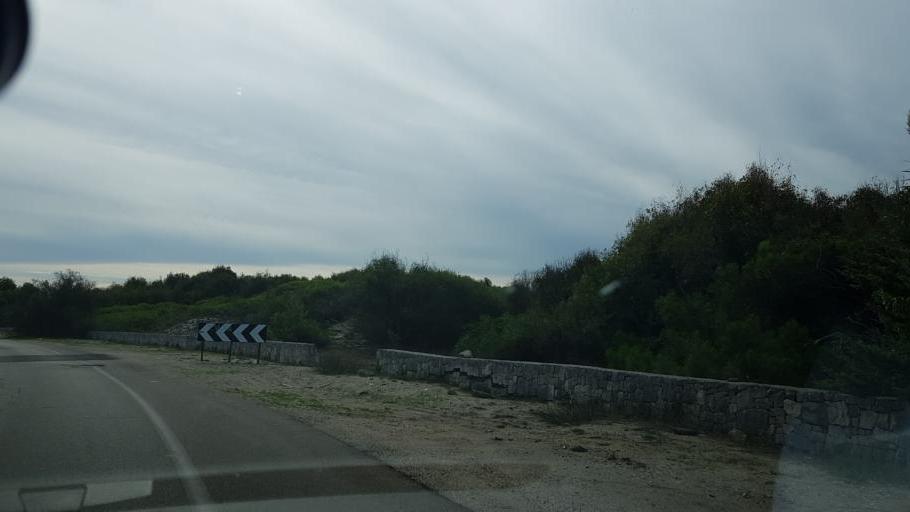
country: IT
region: Apulia
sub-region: Provincia di Lecce
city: Borgagne
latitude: 40.2973
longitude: 18.4100
